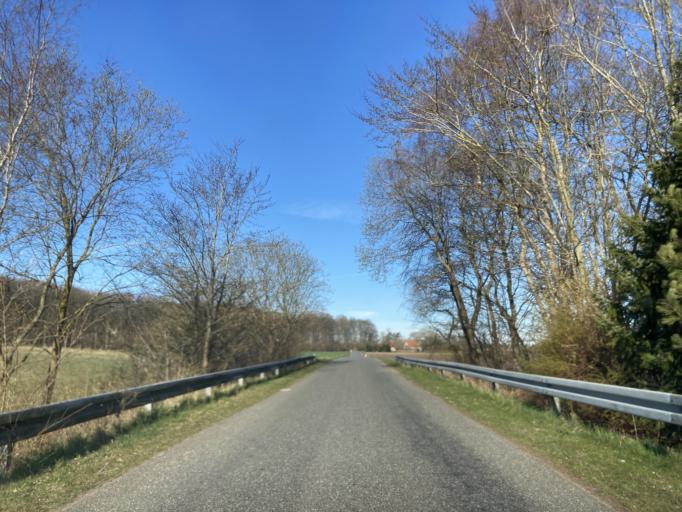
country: DK
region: Zealand
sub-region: Lejre Kommune
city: Kirke Hvalso
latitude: 55.5032
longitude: 11.8590
